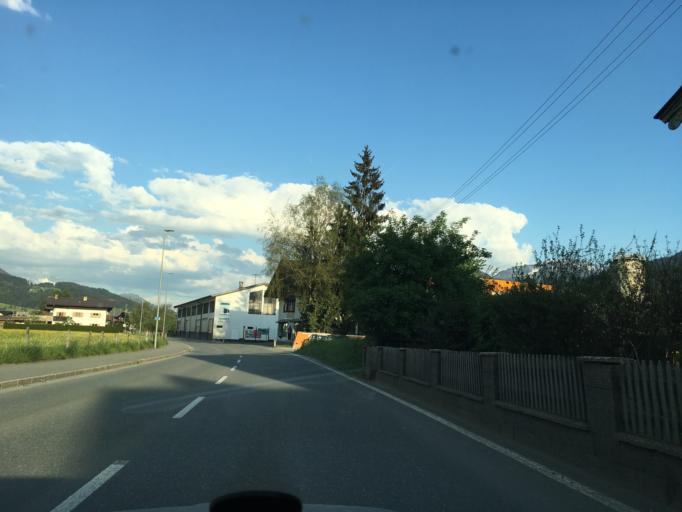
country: AT
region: Tyrol
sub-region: Politischer Bezirk Kitzbuhel
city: Sankt Johann in Tirol
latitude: 47.5210
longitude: 12.4330
